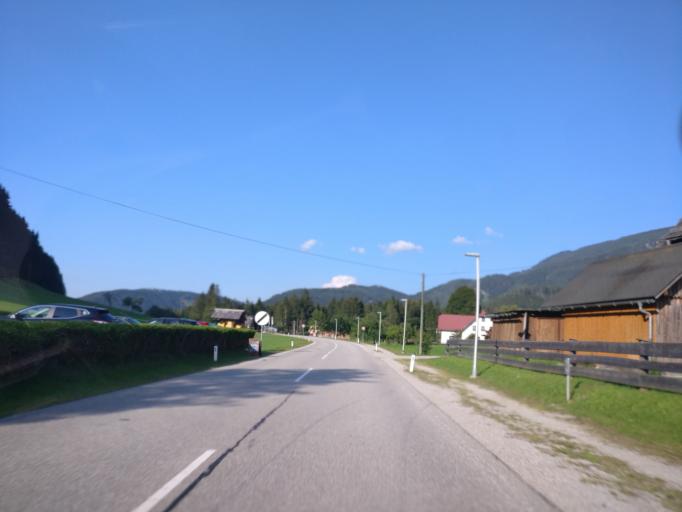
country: AT
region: Lower Austria
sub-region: Politischer Bezirk Scheibbs
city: Gostling an der Ybbs
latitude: 47.7453
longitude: 14.8959
